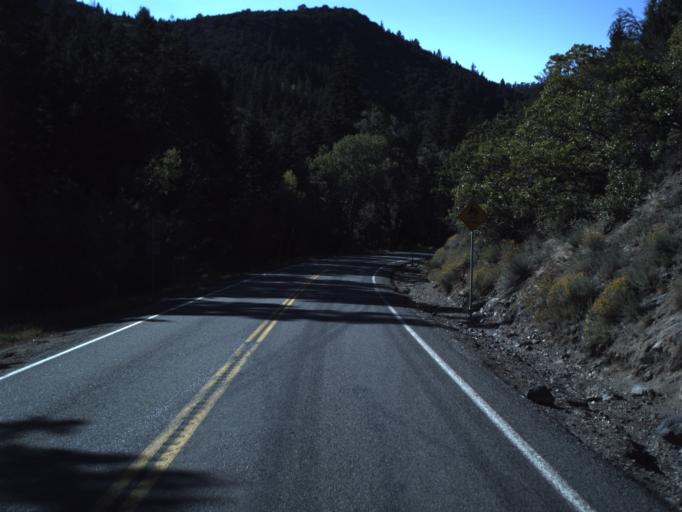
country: US
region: Utah
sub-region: Iron County
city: Parowan
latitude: 37.7566
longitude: -112.8425
